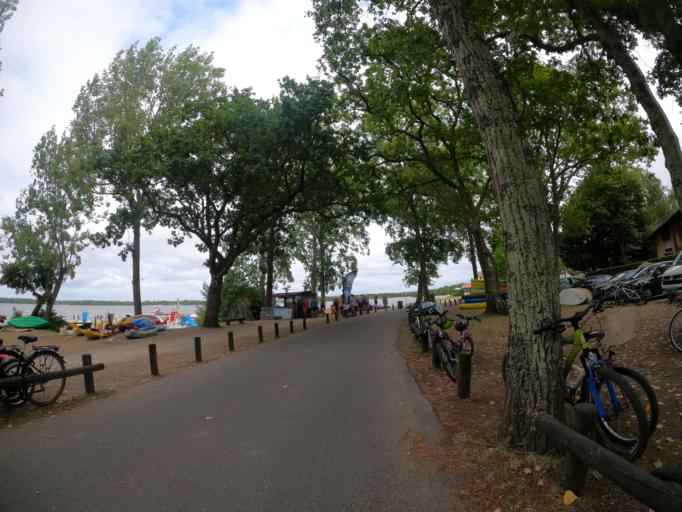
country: FR
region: Aquitaine
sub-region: Departement des Landes
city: Leon
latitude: 43.8874
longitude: -1.3174
